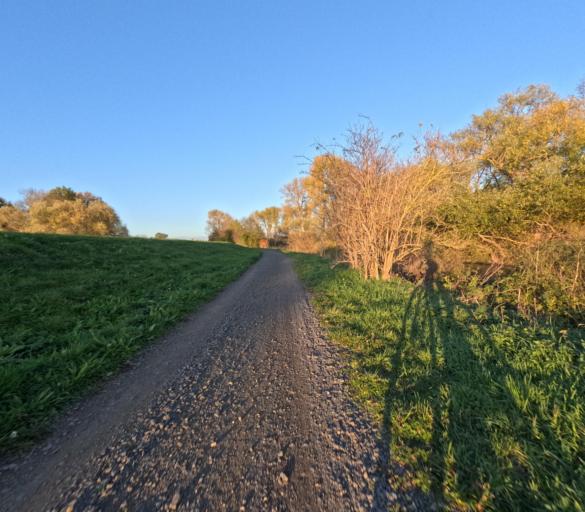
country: DE
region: Saxony-Anhalt
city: Ermlitz
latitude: 51.3832
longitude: 12.1867
